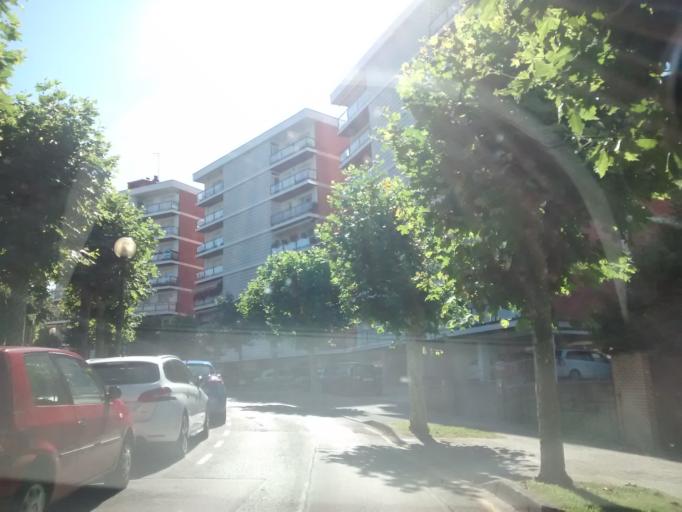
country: ES
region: Cantabria
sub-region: Provincia de Cantabria
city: Santander
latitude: 43.4685
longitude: -3.7840
